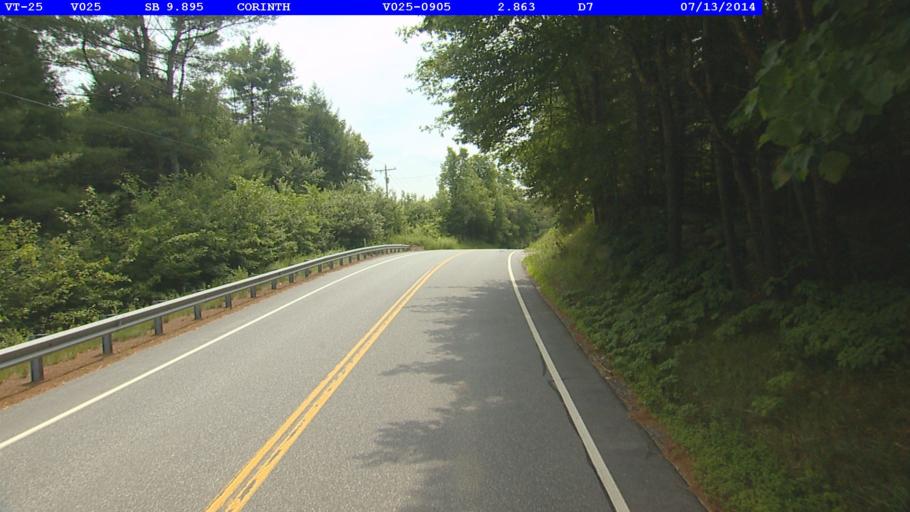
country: US
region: New Hampshire
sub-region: Grafton County
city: Haverhill
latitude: 44.0676
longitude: -72.2449
